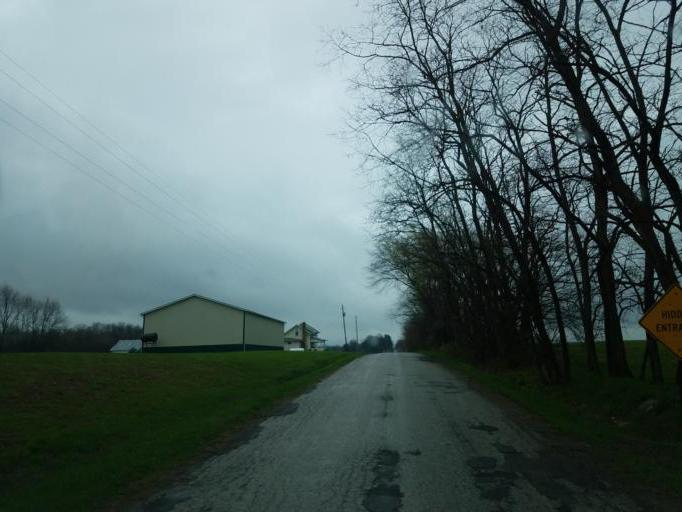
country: US
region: Ohio
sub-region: Morrow County
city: Mount Gilead
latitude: 40.4532
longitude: -82.7457
